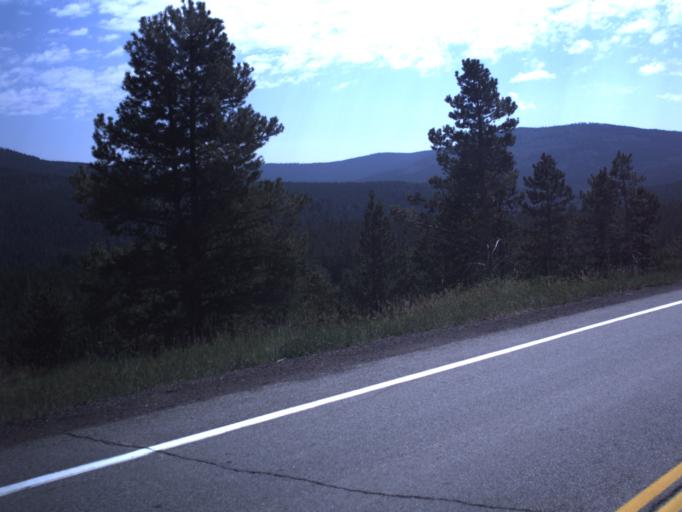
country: US
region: Utah
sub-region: Daggett County
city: Manila
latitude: 40.8354
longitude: -109.4635
